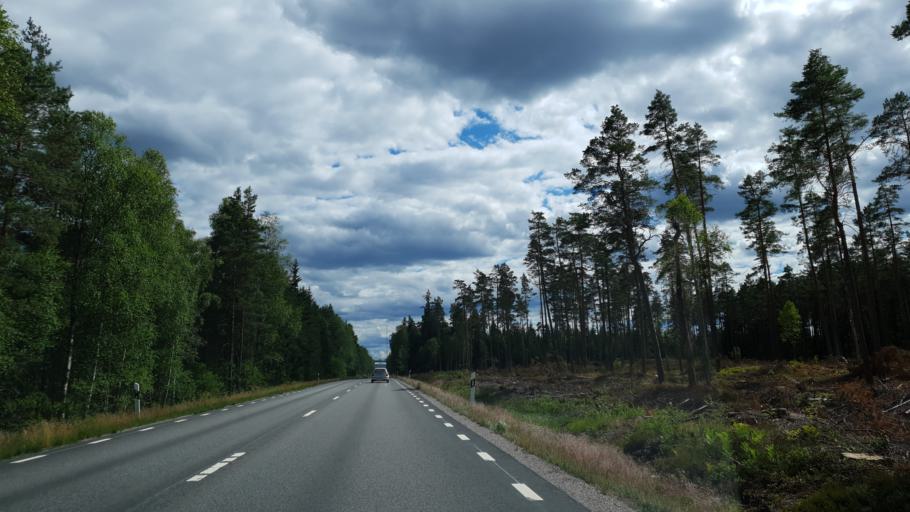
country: SE
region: Kronoberg
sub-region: Lessebo Kommun
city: Lessebo
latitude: 56.7886
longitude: 15.4138
